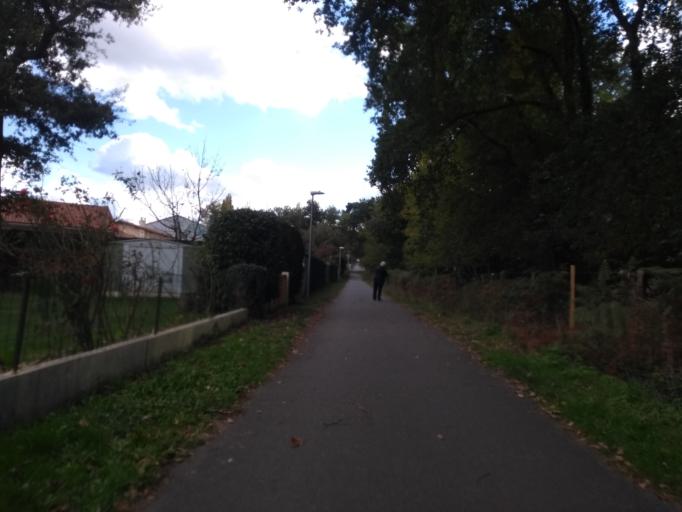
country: FR
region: Aquitaine
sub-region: Departement de la Gironde
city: Canejan
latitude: 44.7572
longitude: -0.6438
